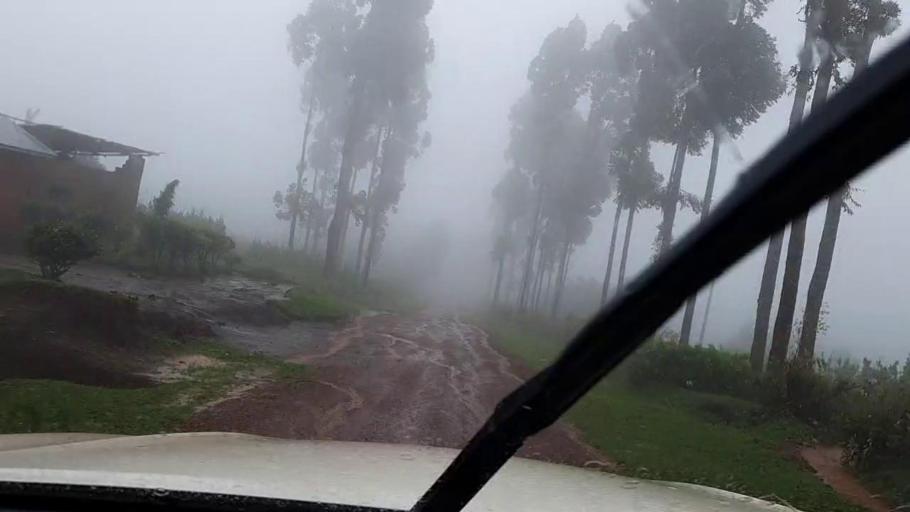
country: RW
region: Northern Province
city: Byumba
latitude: -1.7386
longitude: 30.0097
